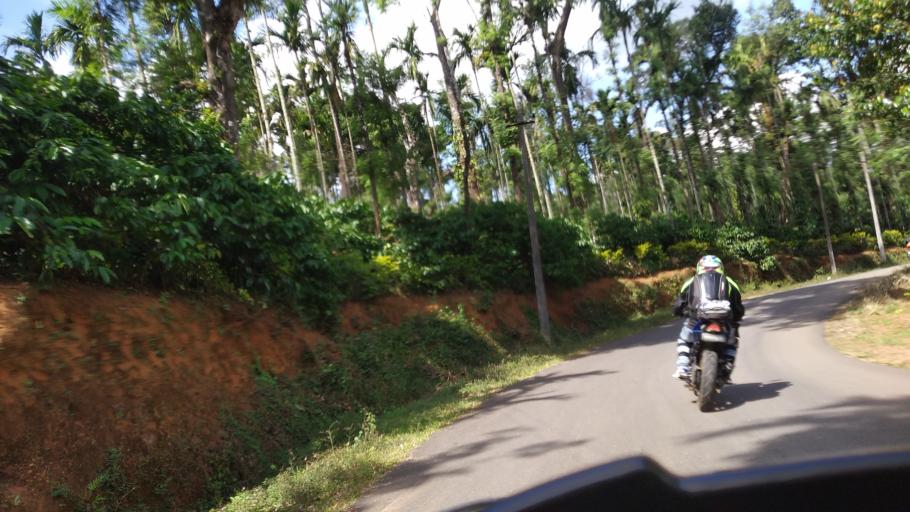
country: IN
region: Karnataka
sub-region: Kodagu
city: Ponnampet
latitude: 12.0345
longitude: 75.9299
